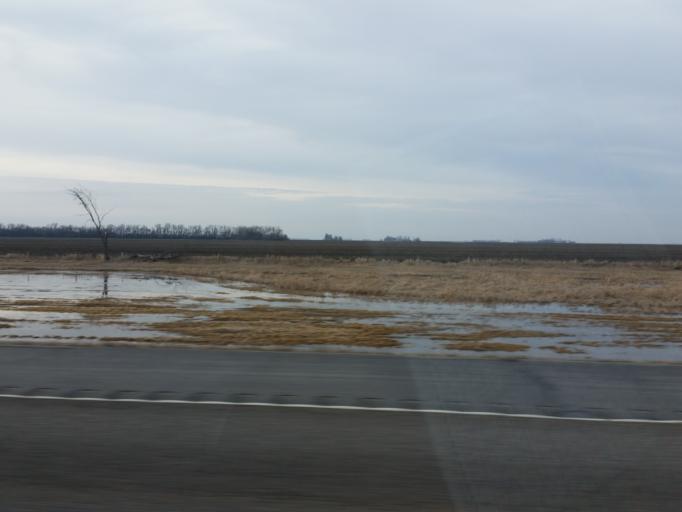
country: US
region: North Dakota
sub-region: Cass County
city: Casselton
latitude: 46.8768
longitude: -97.1658
